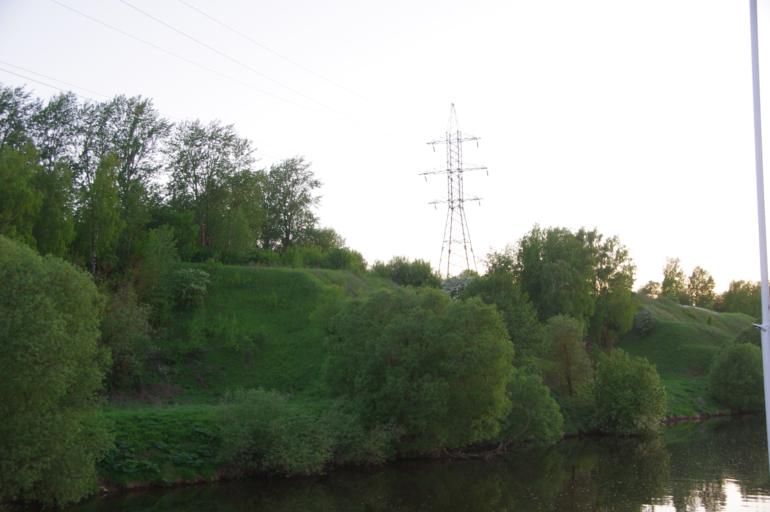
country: RU
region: Moskovskaya
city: Peski
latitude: 55.2337
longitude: 38.7337
